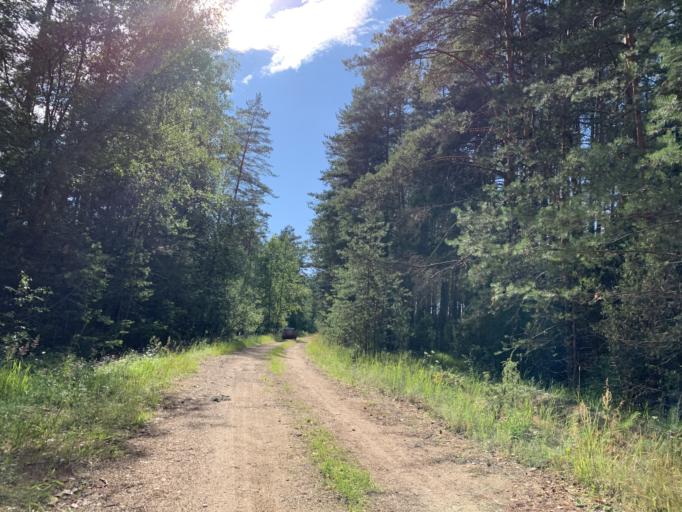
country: BY
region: Minsk
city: Ivyanyets
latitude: 53.9714
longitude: 26.8044
